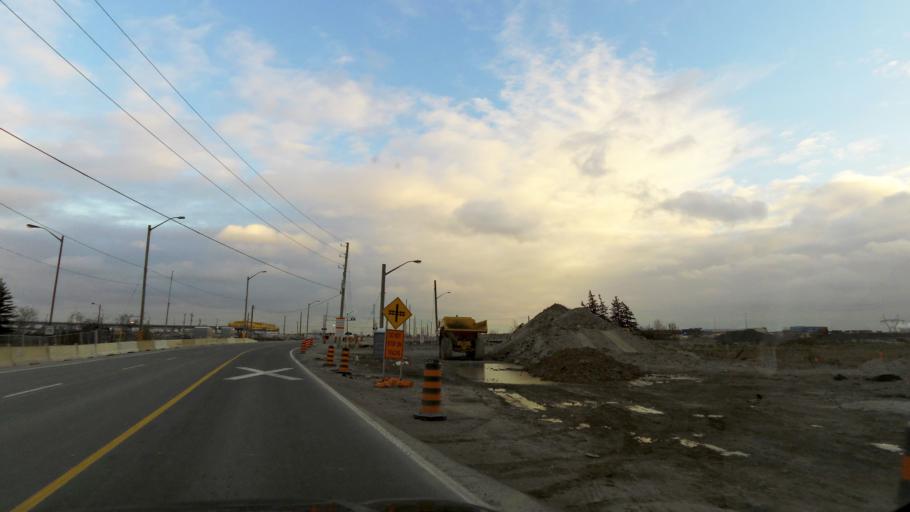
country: CA
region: Ontario
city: Brampton
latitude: 43.7092
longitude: -79.6727
